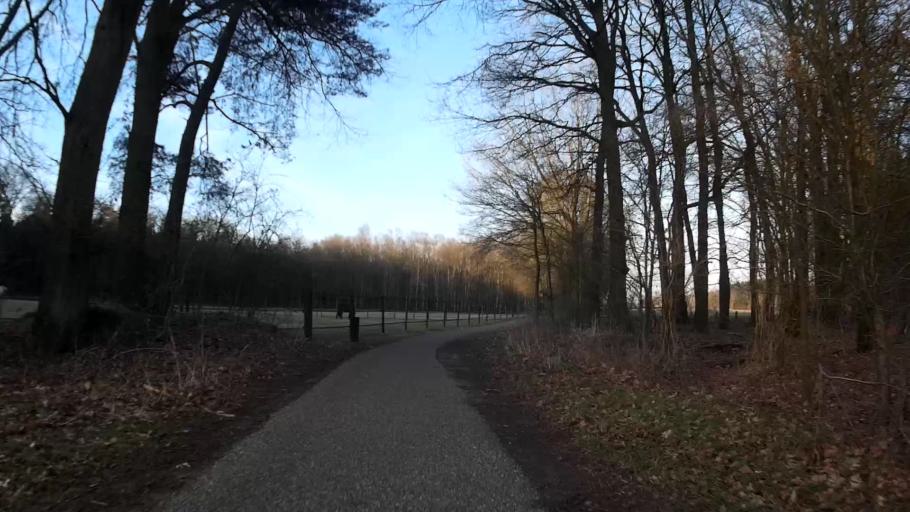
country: NL
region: Utrecht
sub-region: Gemeente Utrechtse Heuvelrug
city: Overberg
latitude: 52.0117
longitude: 5.5180
